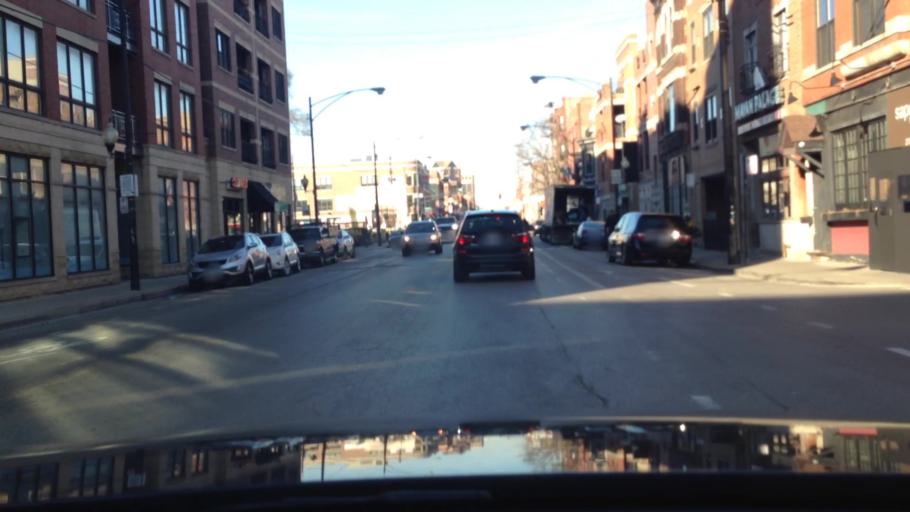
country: US
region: Illinois
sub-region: Cook County
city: Chicago
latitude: 41.9314
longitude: -87.6490
